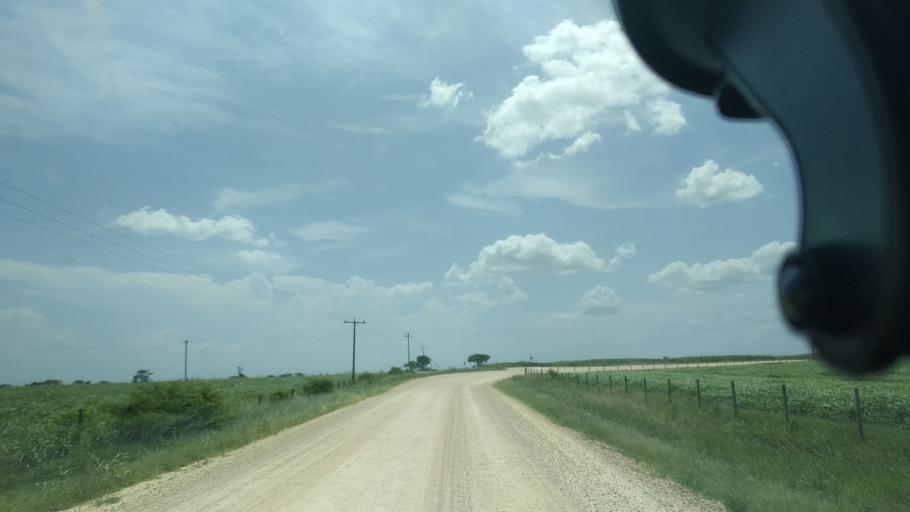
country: BZ
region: Cayo
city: San Ignacio
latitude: 17.3149
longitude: -89.0462
